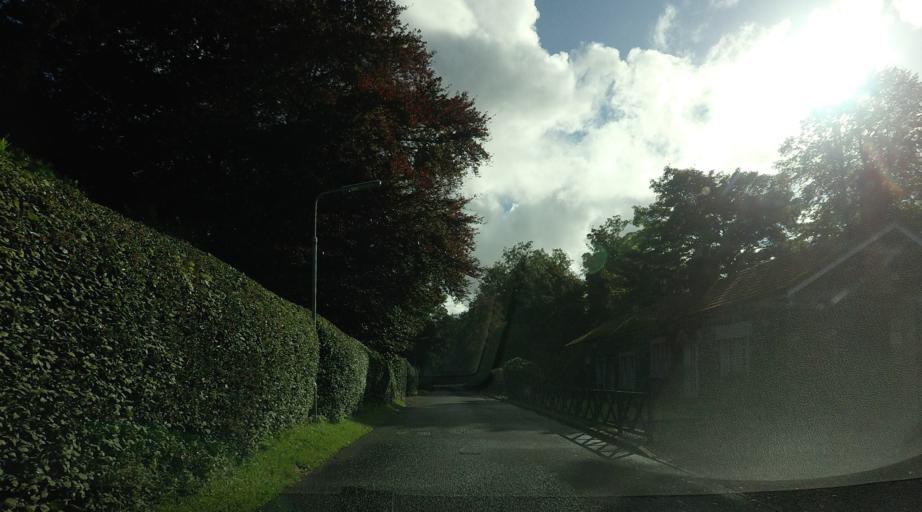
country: GB
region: Scotland
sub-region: Fife
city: Balmullo
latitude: 56.3842
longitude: -2.9952
